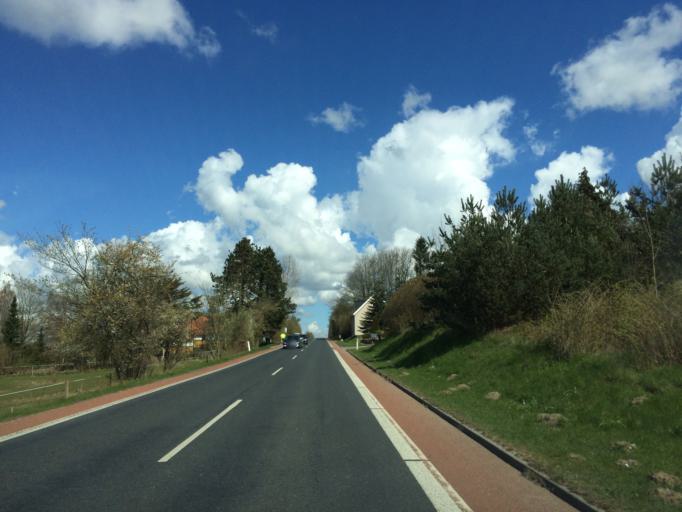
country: DK
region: South Denmark
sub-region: Assens Kommune
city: Harby
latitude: 55.1839
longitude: 10.1537
